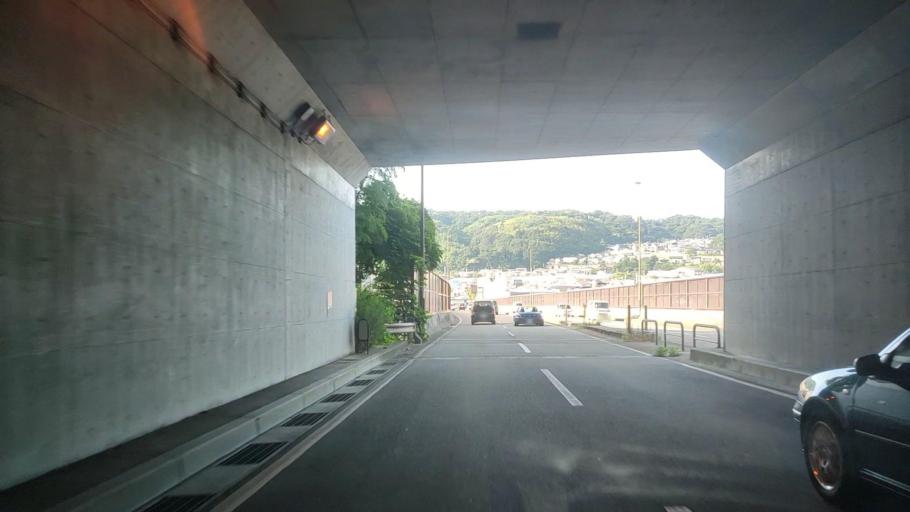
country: JP
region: Ishikawa
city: Kanazawa-shi
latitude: 36.5575
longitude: 136.6766
